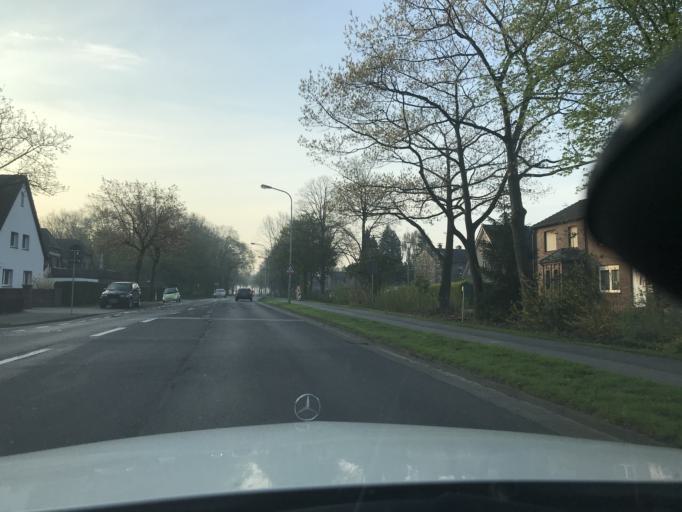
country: DE
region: North Rhine-Westphalia
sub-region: Regierungsbezirk Dusseldorf
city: Moers
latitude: 51.4125
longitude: 6.5959
